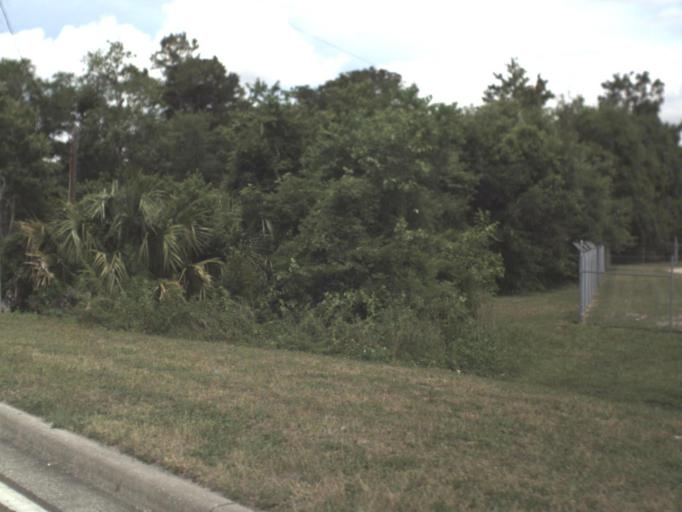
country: US
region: Florida
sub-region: Duval County
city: Jacksonville
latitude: 30.4074
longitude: -81.6386
